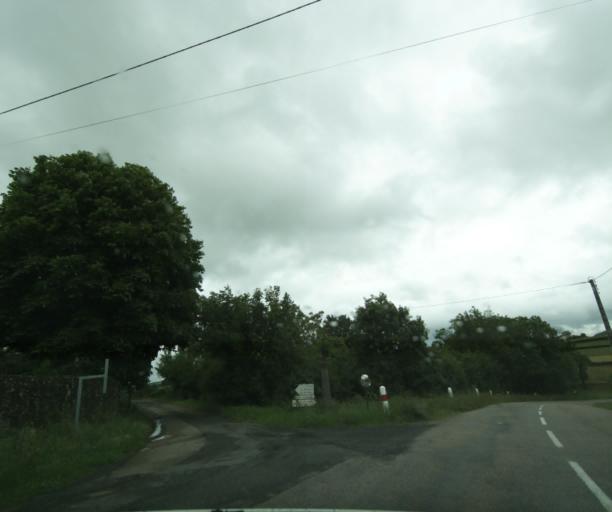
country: FR
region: Bourgogne
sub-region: Departement de Saone-et-Loire
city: Matour
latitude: 46.4228
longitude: 4.4525
